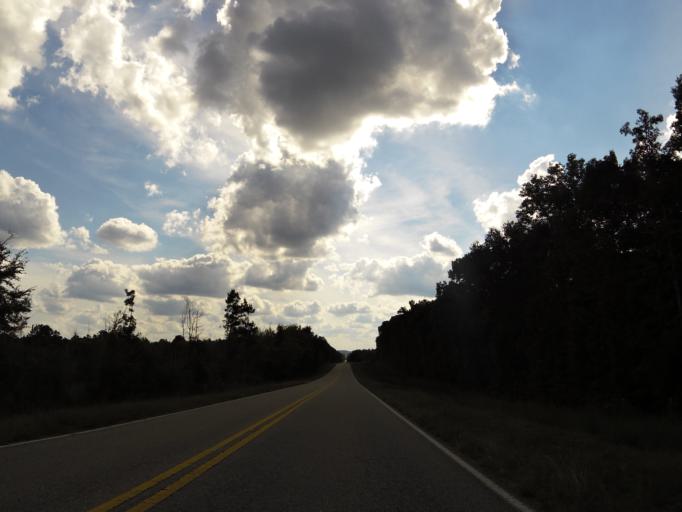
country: US
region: Alabama
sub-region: Dallas County
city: Selmont-West Selmont
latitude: 32.2132
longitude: -87.0062
